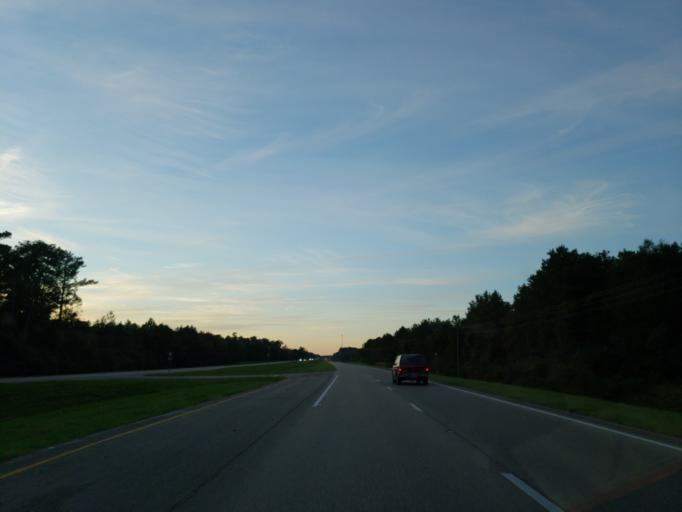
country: US
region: Mississippi
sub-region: Wayne County
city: Belmont
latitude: 31.6026
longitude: -88.5589
